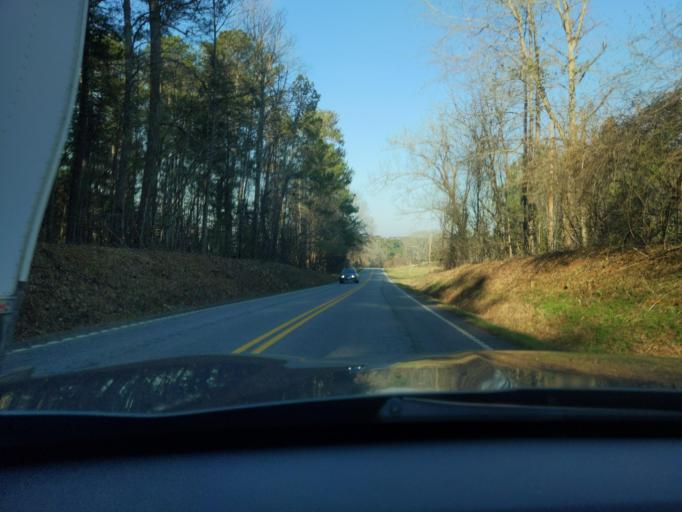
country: US
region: South Carolina
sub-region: Greenwood County
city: Ninety Six
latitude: 34.1736
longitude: -82.0871
